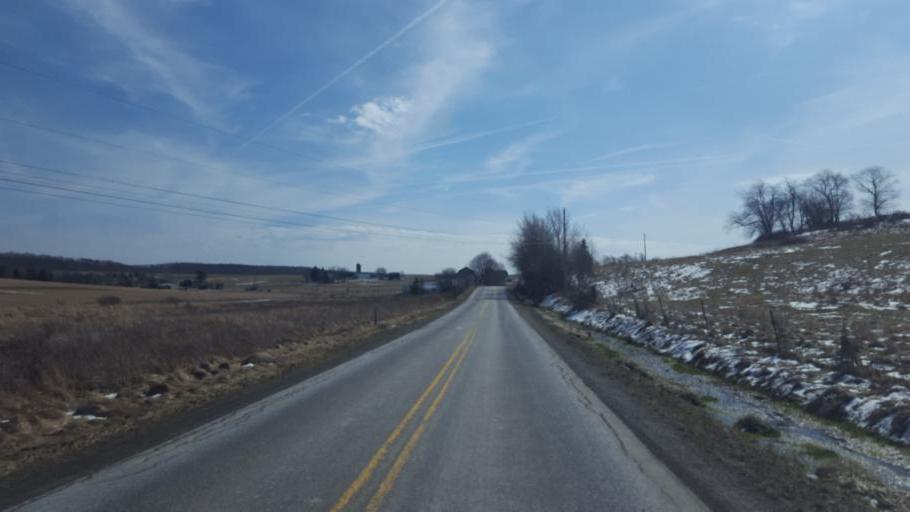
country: US
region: Pennsylvania
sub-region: Potter County
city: Galeton
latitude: 41.8924
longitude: -77.7454
